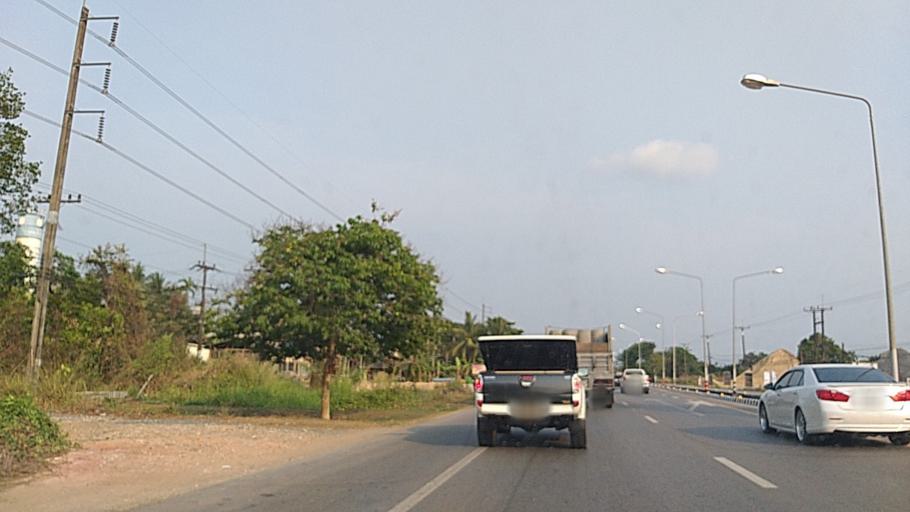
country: TH
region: Chanthaburi
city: Khlung
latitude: 12.4570
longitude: 102.2354
